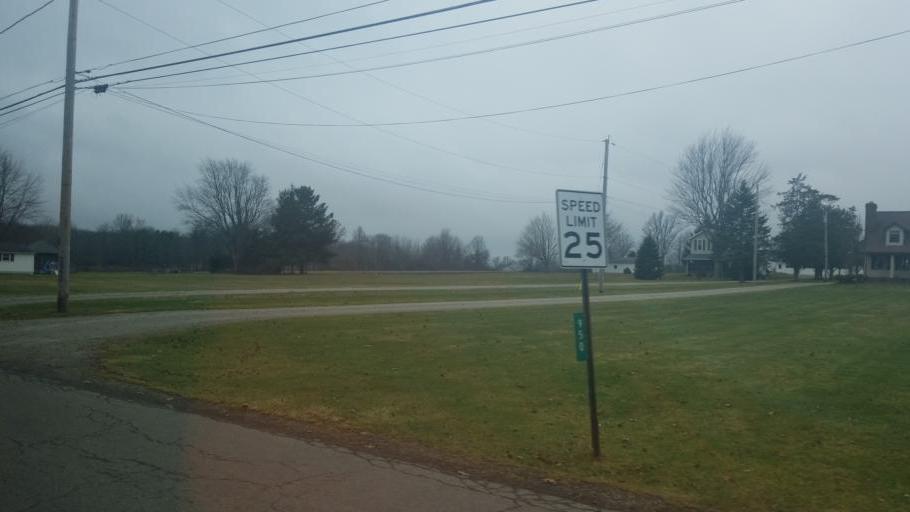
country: US
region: Ohio
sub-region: Crawford County
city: Galion
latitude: 40.7167
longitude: -82.7931
